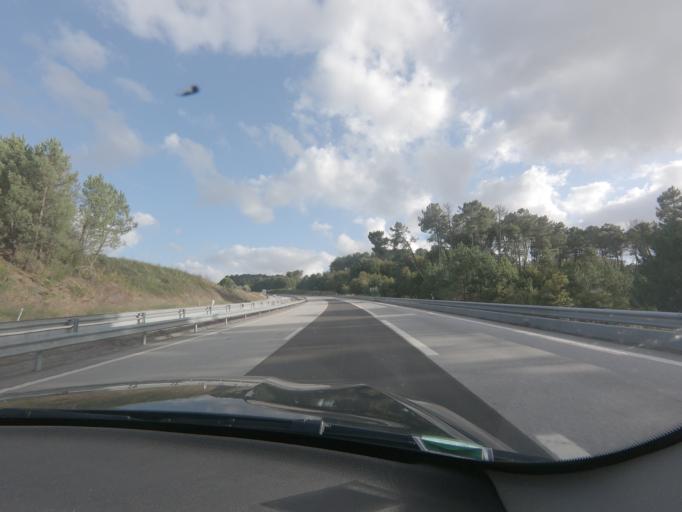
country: PT
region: Viseu
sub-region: Viseu
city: Campo
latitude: 40.7393
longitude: -7.9245
